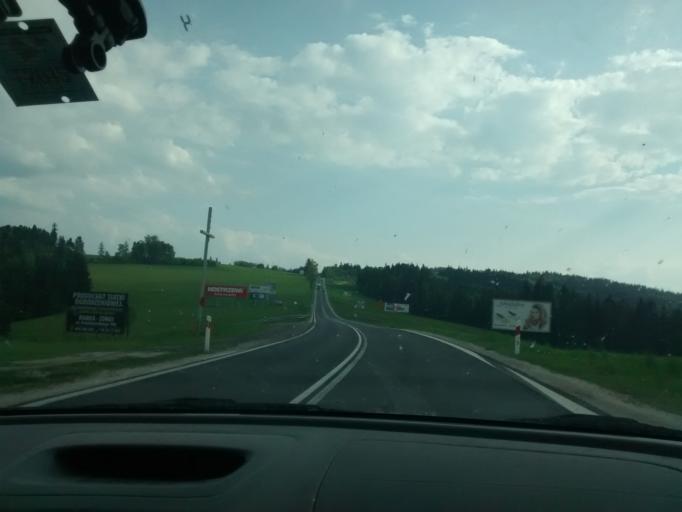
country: PL
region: Lesser Poland Voivodeship
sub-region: Powiat nowotarski
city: Rokiciny
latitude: 49.5690
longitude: 19.9461
